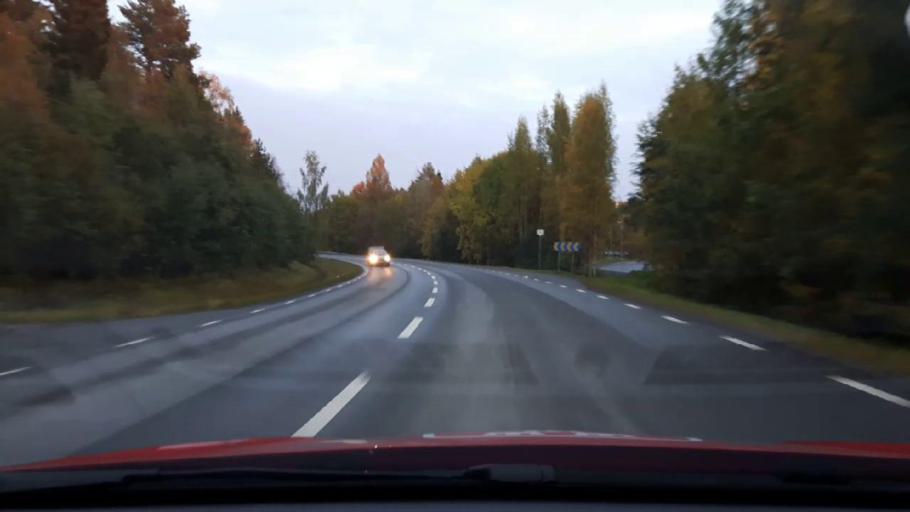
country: SE
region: Jaemtland
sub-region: OEstersunds Kommun
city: Ostersund
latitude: 63.2113
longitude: 14.6269
